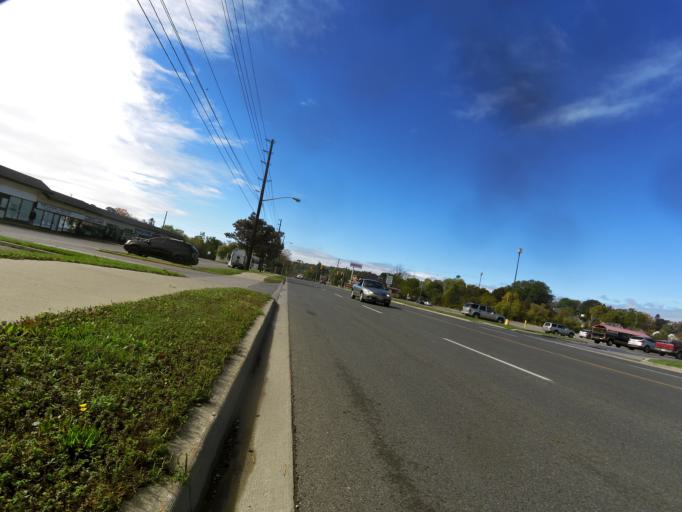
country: CA
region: Ontario
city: Cobourg
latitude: 43.9498
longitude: -78.2840
